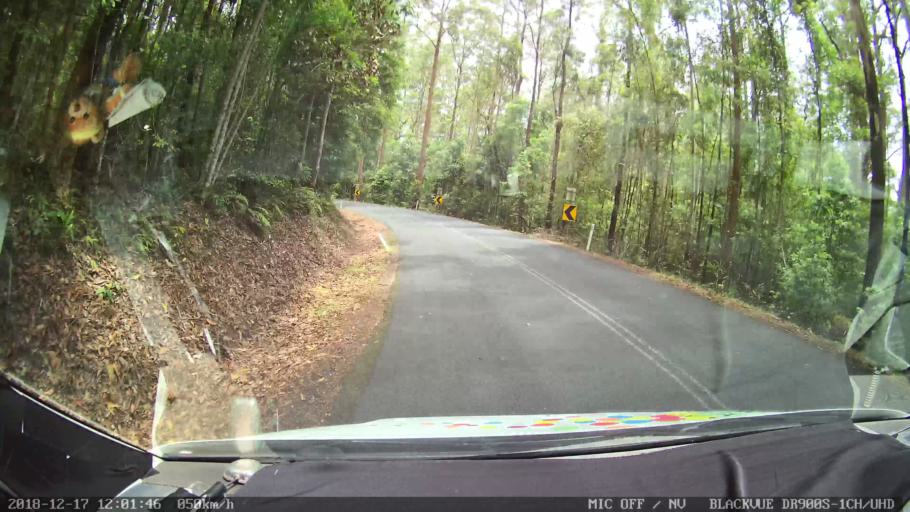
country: AU
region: New South Wales
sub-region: Kyogle
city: Kyogle
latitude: -28.5194
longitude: 152.5716
